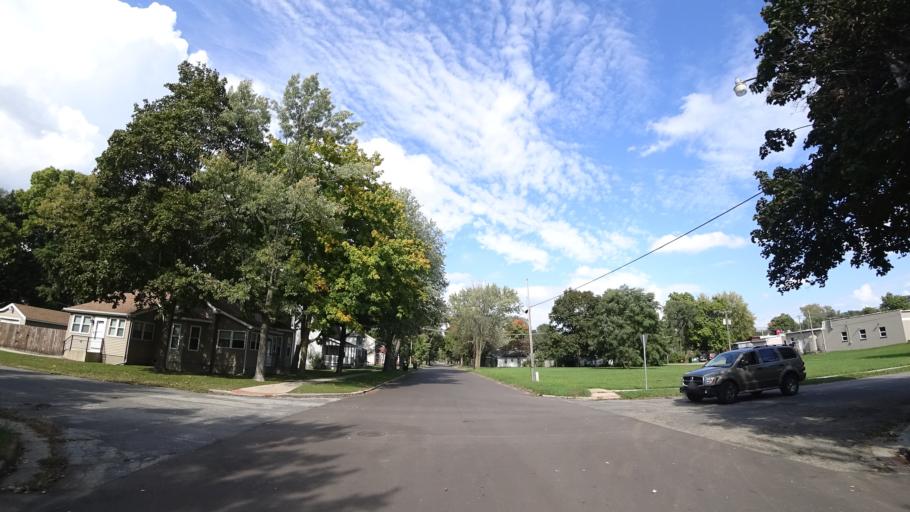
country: US
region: Michigan
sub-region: Saint Joseph County
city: Three Rivers
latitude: 41.9301
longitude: -85.6283
